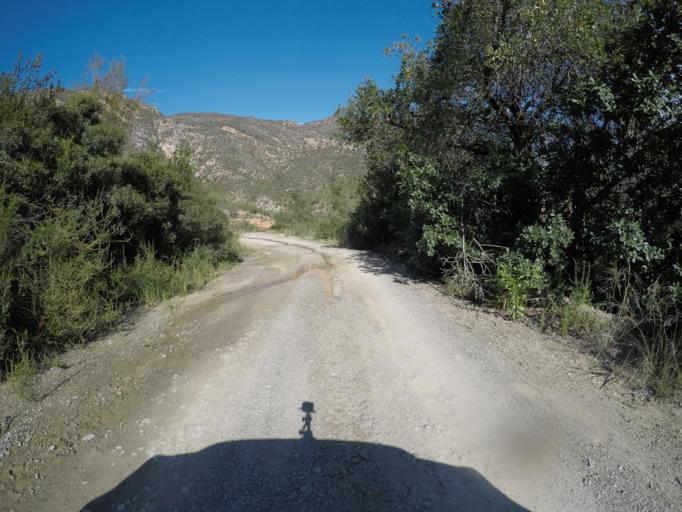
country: ZA
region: Eastern Cape
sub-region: Cacadu District Municipality
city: Kareedouw
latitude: -33.6464
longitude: 24.4561
